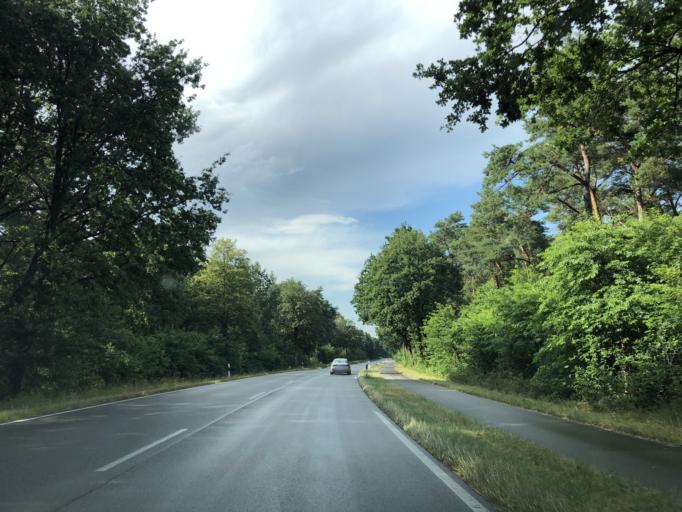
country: DE
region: North Rhine-Westphalia
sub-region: Regierungsbezirk Dusseldorf
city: Kranenburg
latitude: 51.7255
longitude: 6.0369
